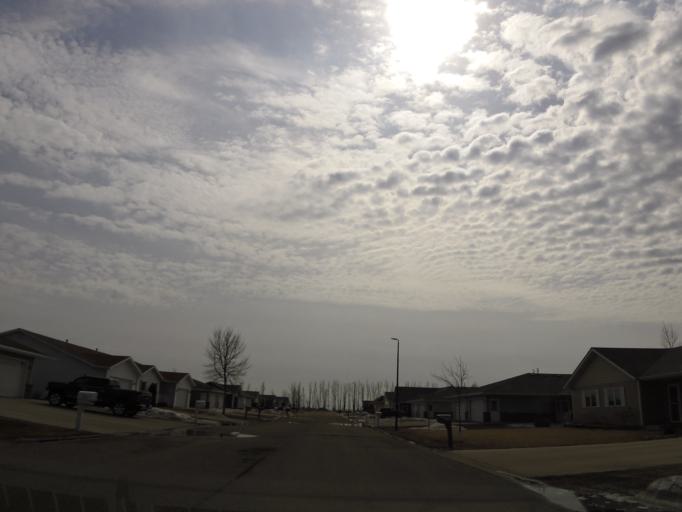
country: US
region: North Dakota
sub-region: Walsh County
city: Grafton
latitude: 48.4079
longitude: -97.4279
